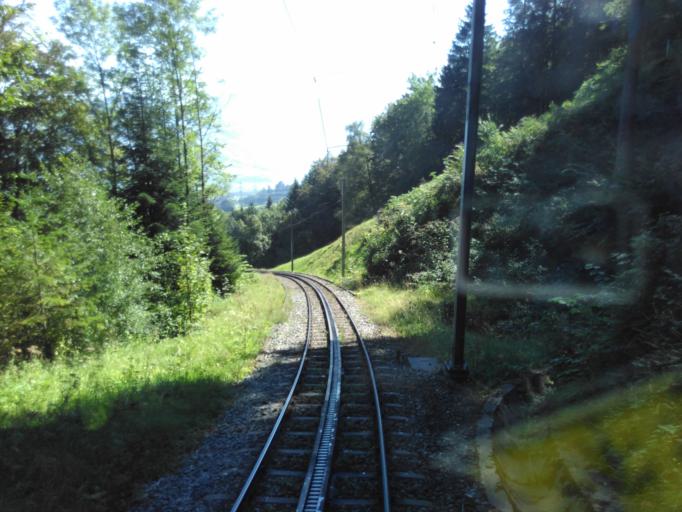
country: CH
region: Schwyz
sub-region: Bezirk Schwyz
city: Goldau
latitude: 47.0386
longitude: 8.5255
